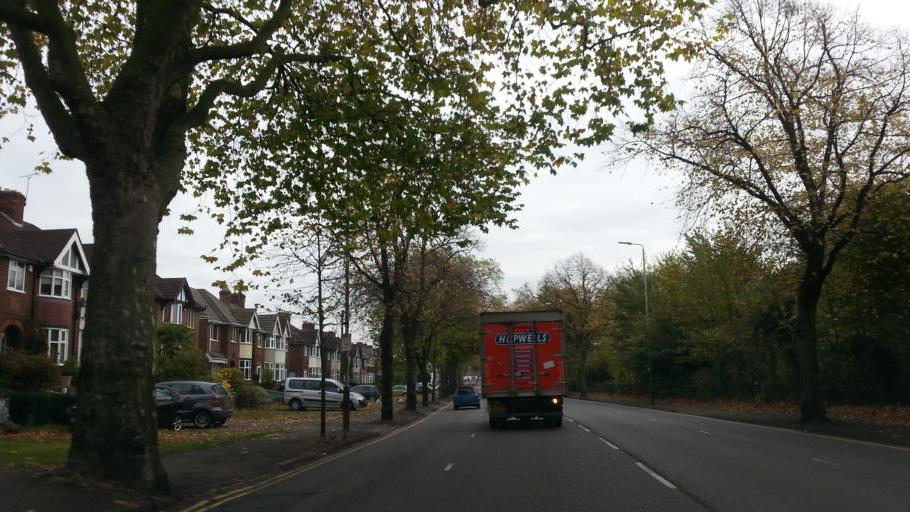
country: GB
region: England
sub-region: City of Leicester
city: Leicester
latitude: 52.6448
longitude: -1.1552
